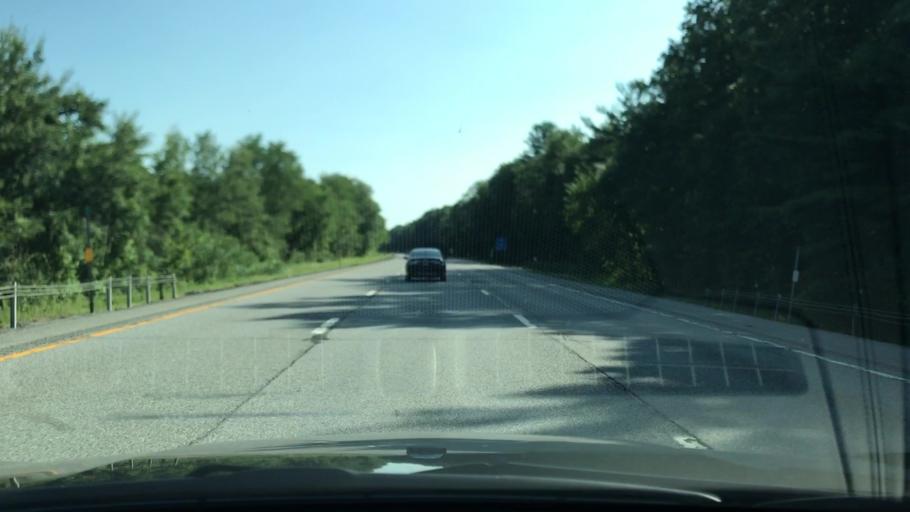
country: US
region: New York
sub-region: Saratoga County
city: Saratoga Springs
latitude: 43.1635
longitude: -73.7174
